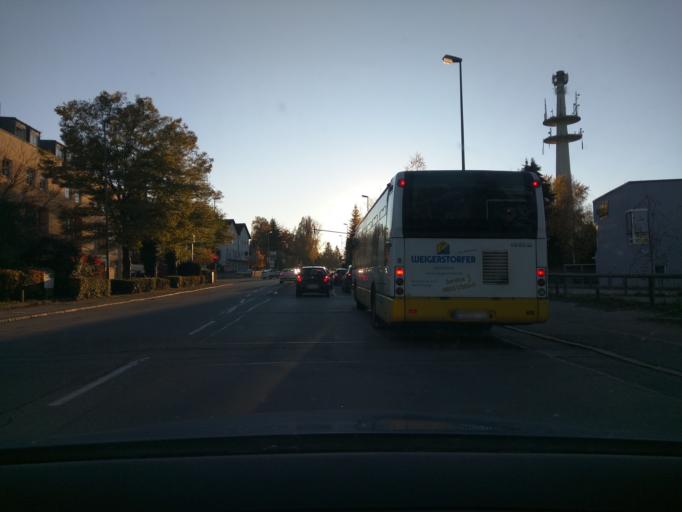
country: DE
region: Bavaria
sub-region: Lower Bavaria
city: Passau
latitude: 48.5658
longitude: 13.4359
